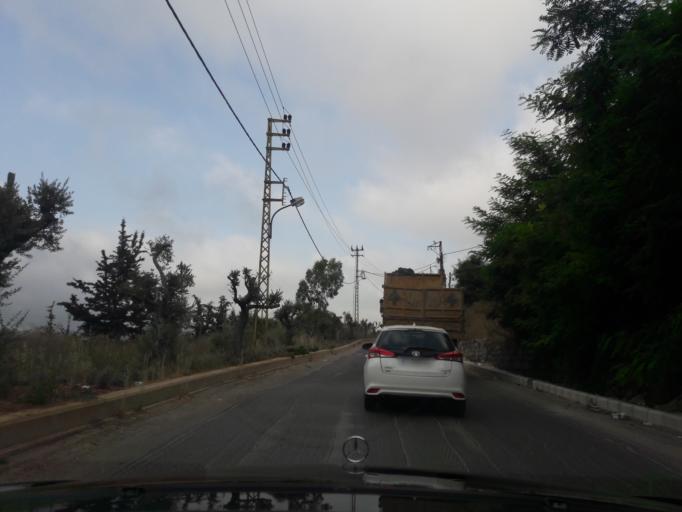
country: LB
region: Mont-Liban
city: Djounie
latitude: 33.9230
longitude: 35.7313
